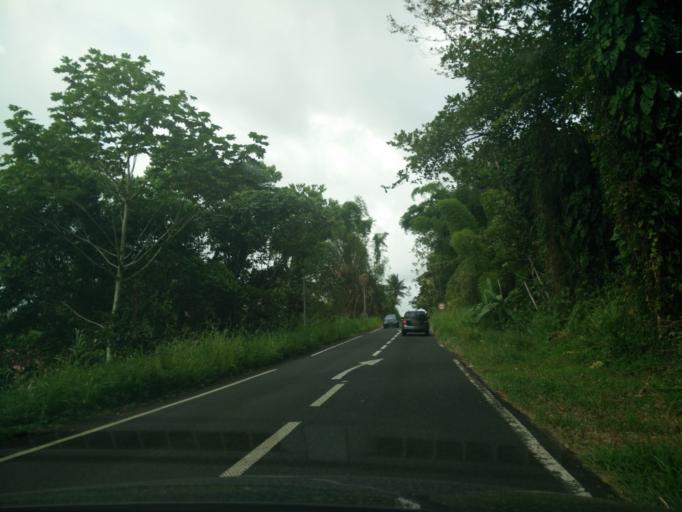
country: GP
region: Guadeloupe
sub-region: Guadeloupe
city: Petit-Bourg
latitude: 16.1927
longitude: -61.6565
